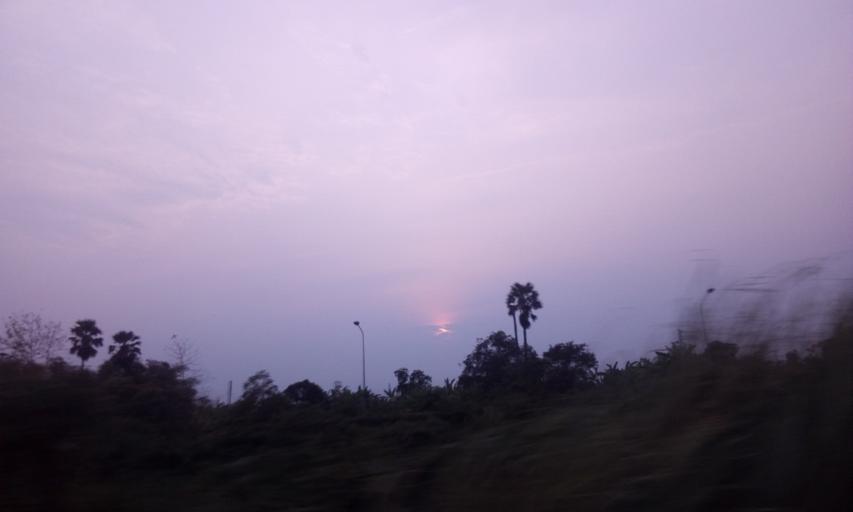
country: TH
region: Pathum Thani
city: Nong Suea
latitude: 14.0384
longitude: 100.8936
